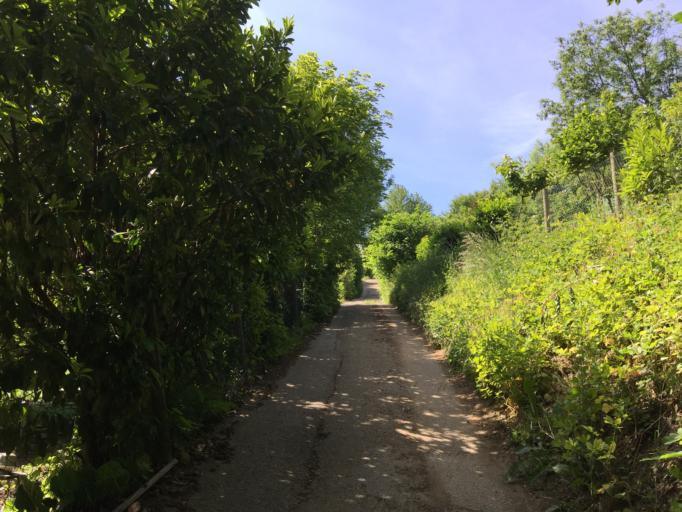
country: FR
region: Rhone-Alpes
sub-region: Departement de la Loire
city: Saint-Priest-en-Jarez
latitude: 45.4544
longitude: 4.3755
